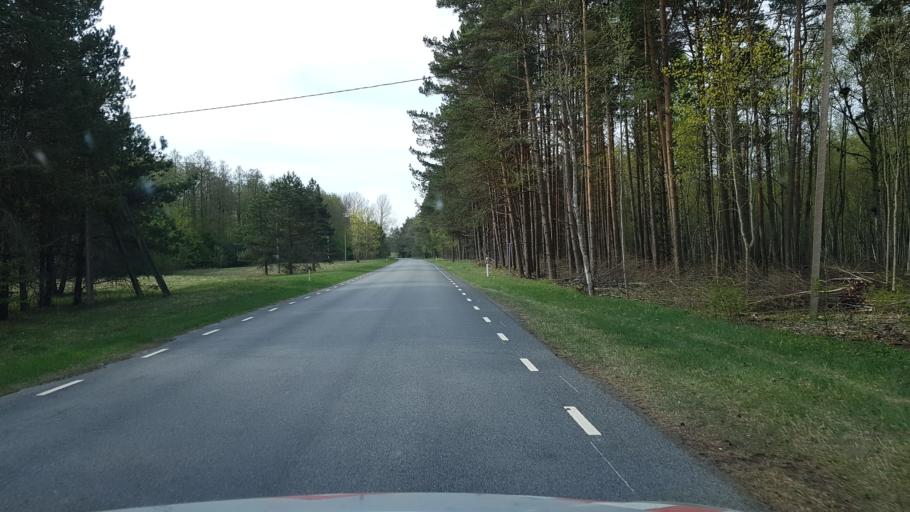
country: EE
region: Paernumaa
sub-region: Audru vald
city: Audru
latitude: 58.3559
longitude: 24.2566
